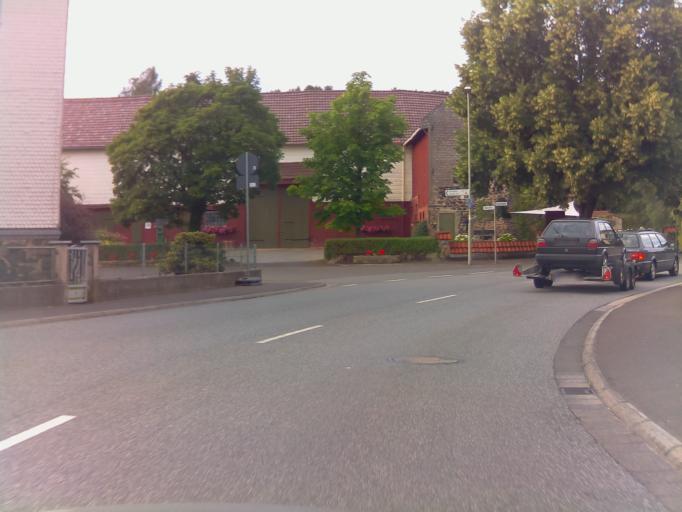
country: DE
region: Hesse
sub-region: Regierungsbezirk Kassel
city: Ottrau
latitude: 50.7506
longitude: 9.3462
